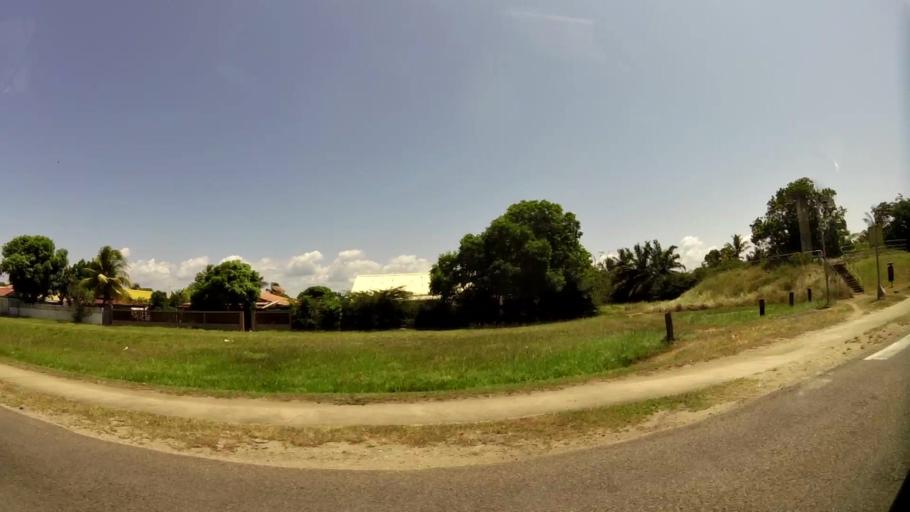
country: GF
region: Guyane
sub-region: Guyane
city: Kourou
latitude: 5.1696
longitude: -52.6471
